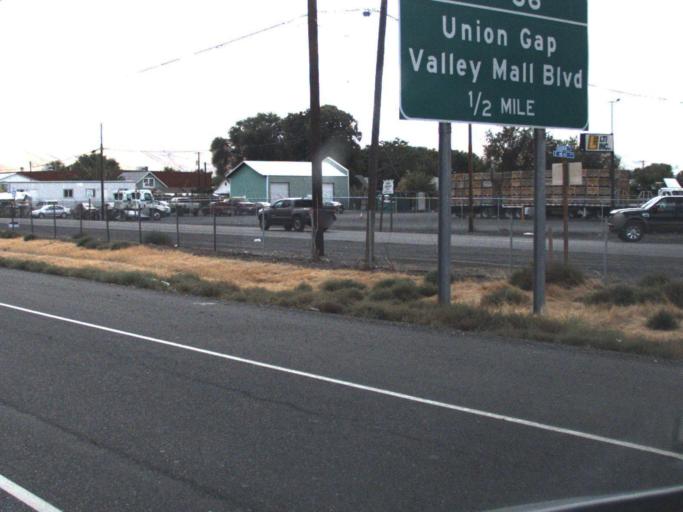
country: US
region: Washington
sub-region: Yakima County
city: Union Gap
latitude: 46.5777
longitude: -120.4720
